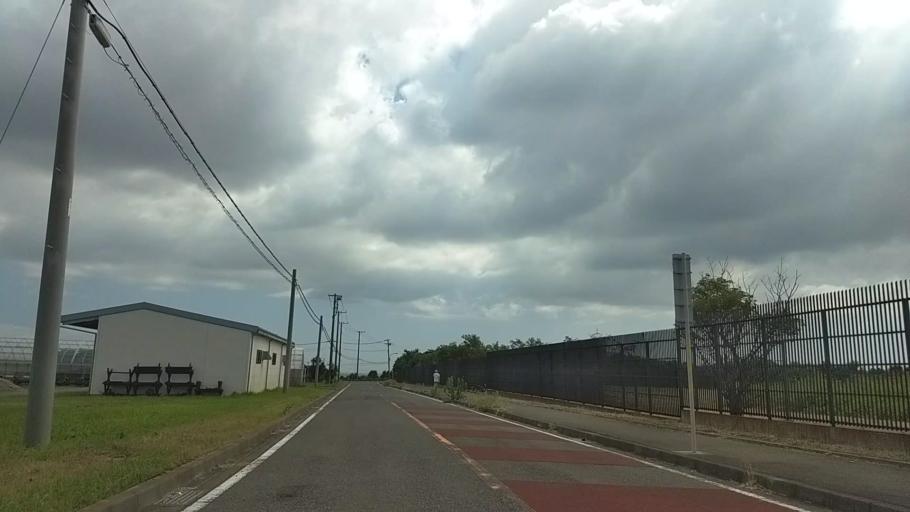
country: JP
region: Kanagawa
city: Miura
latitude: 35.1947
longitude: 139.6148
